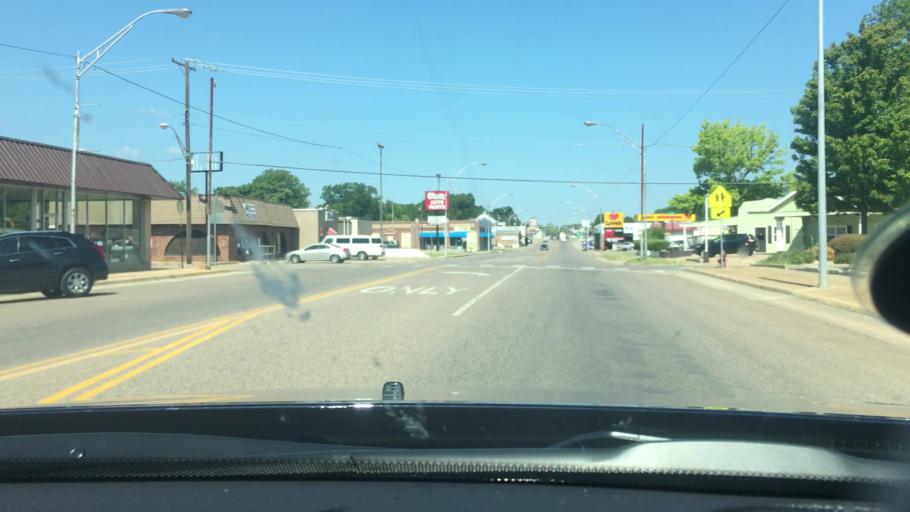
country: US
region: Oklahoma
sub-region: Bryan County
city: Durant
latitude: 33.9918
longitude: -96.3805
